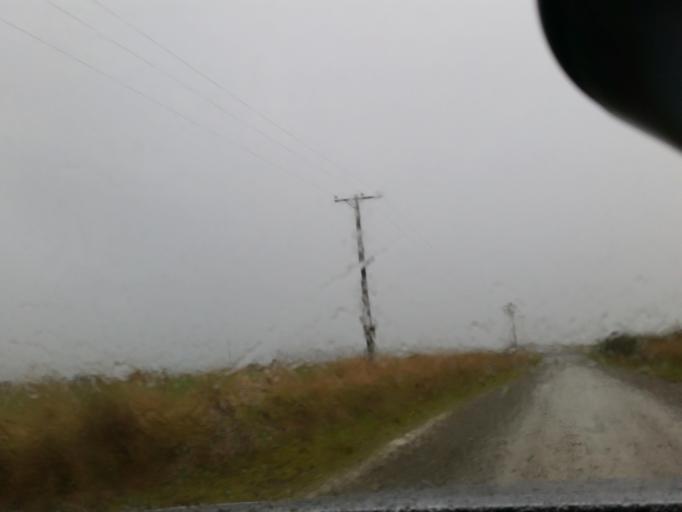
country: NZ
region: Southland
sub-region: Southland District
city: Winton
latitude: -46.2508
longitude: 168.4568
